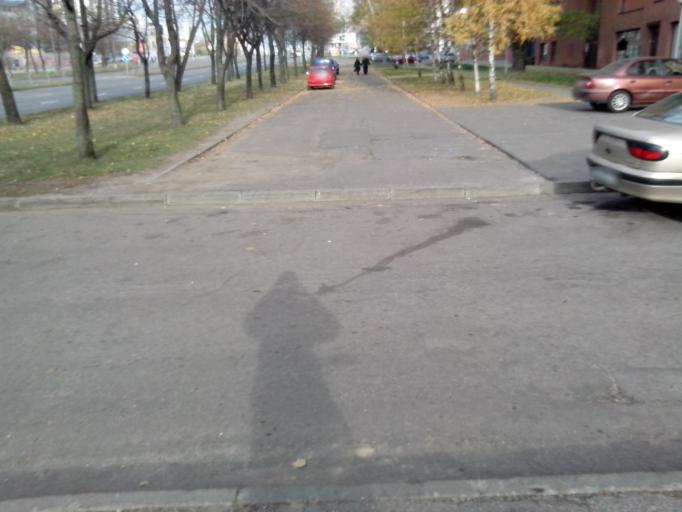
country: BY
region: Minsk
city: Minsk
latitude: 53.9342
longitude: 27.5807
